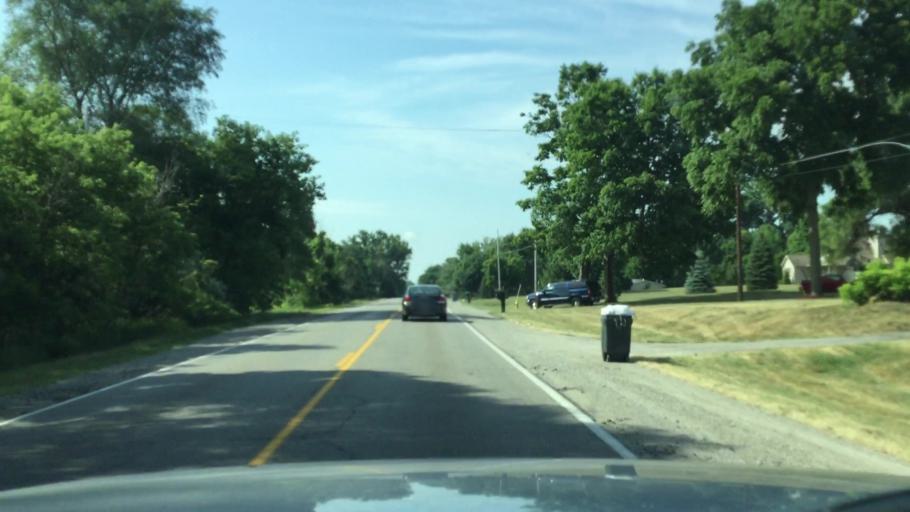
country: US
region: Michigan
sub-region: Genesee County
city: Flushing
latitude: 43.1015
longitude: -83.8137
